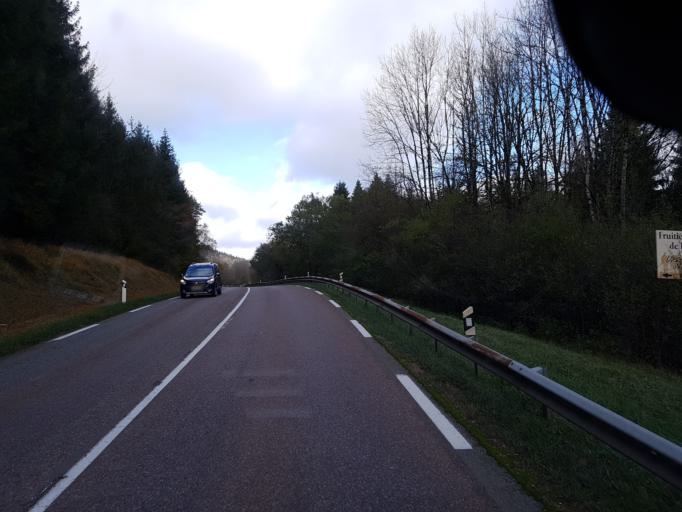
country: FR
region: Franche-Comte
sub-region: Departement du Jura
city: Champagnole
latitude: 46.6866
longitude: 5.9304
